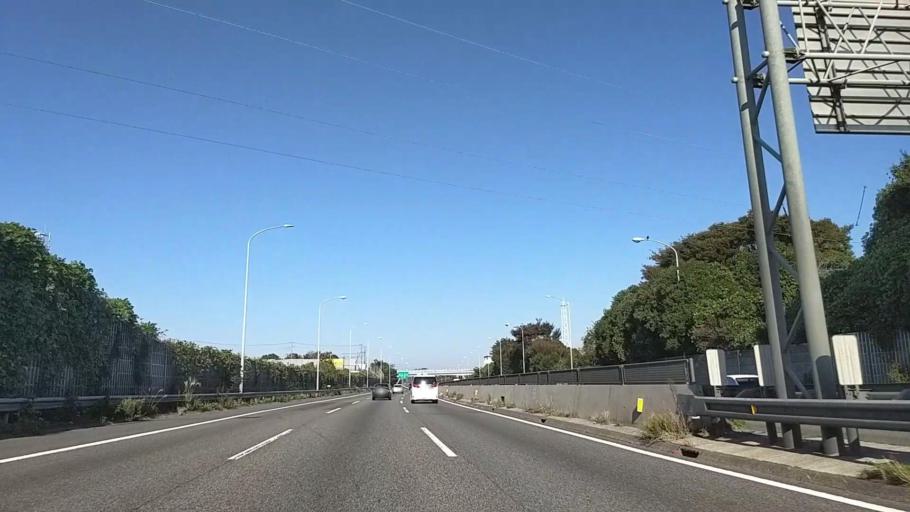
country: JP
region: Kanagawa
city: Yokohama
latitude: 35.4578
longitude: 139.5472
